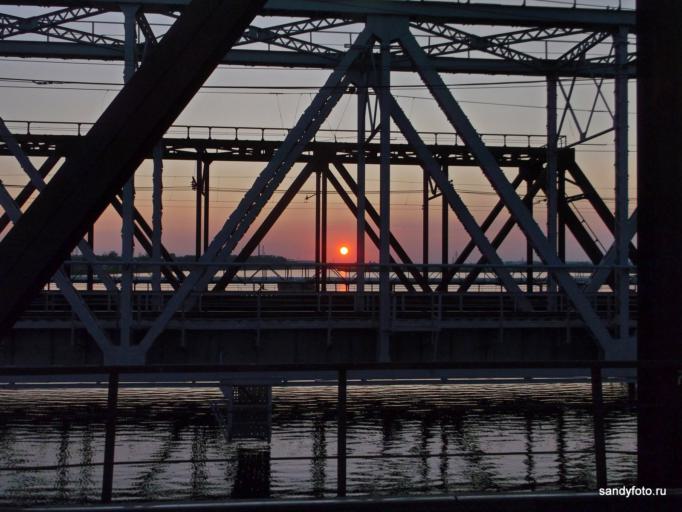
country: RU
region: Chelyabinsk
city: Troitsk
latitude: 54.0553
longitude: 61.6115
